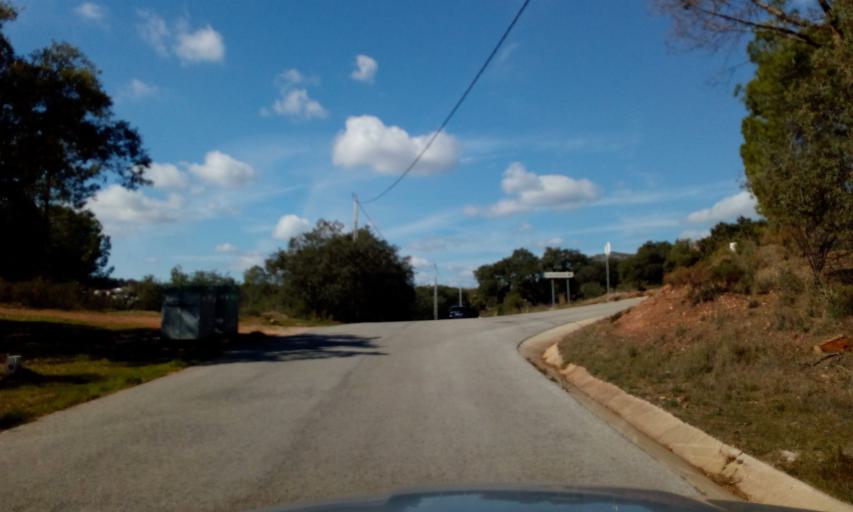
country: PT
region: Faro
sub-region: Loule
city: Loule
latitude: 37.2465
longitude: -8.0812
